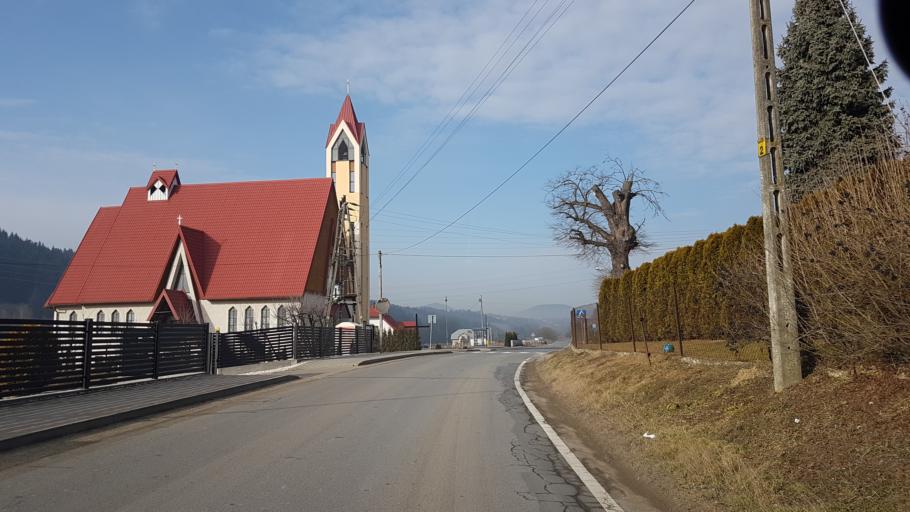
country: PL
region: Lesser Poland Voivodeship
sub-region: Powiat nowosadecki
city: Olszana
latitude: 49.5638
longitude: 20.5544
